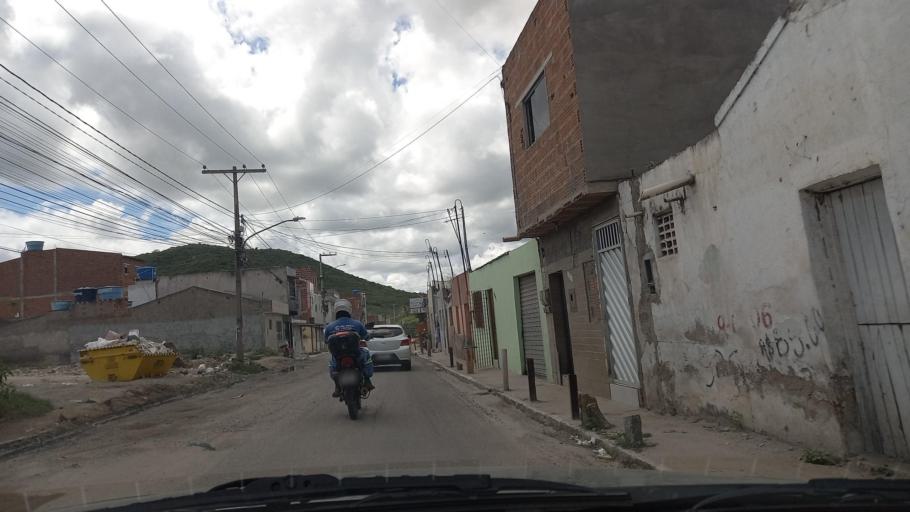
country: BR
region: Pernambuco
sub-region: Caruaru
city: Caruaru
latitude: -8.2786
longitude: -35.9444
